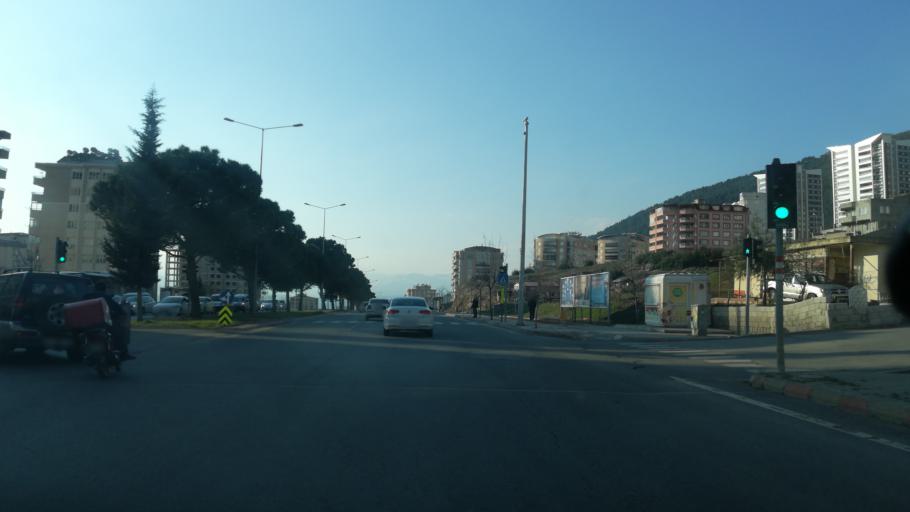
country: TR
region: Kahramanmaras
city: Kahramanmaras
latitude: 37.5957
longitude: 36.8515
